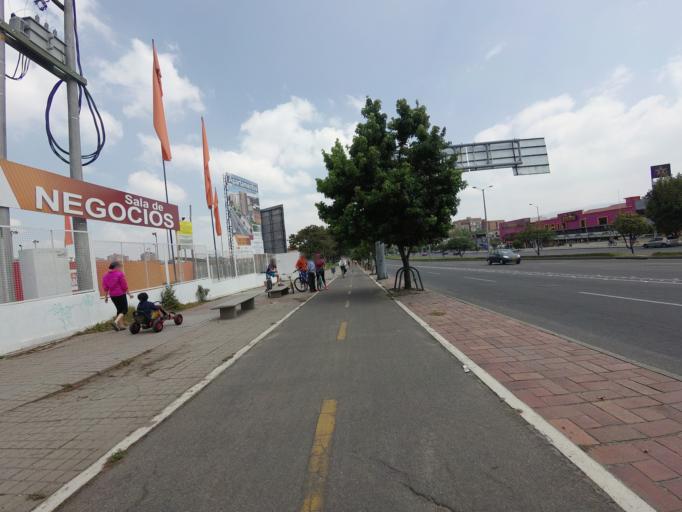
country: CO
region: Bogota D.C.
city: Barrio San Luis
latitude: 4.7243
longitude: -74.0730
